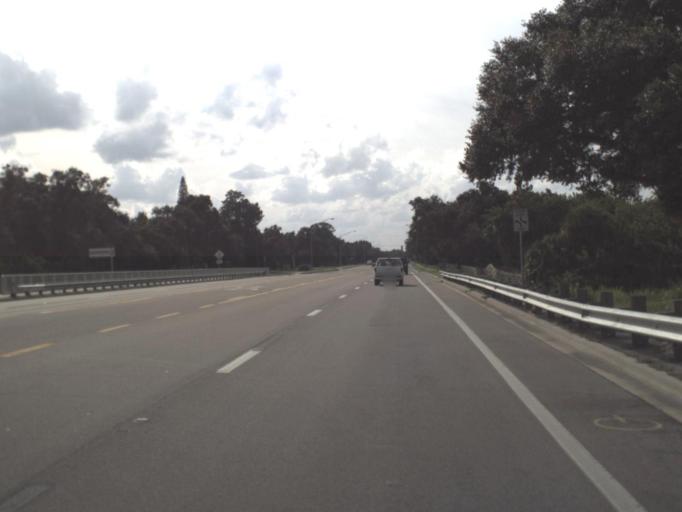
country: US
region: Florida
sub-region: Hendry County
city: LaBelle
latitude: 26.7620
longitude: -81.4216
